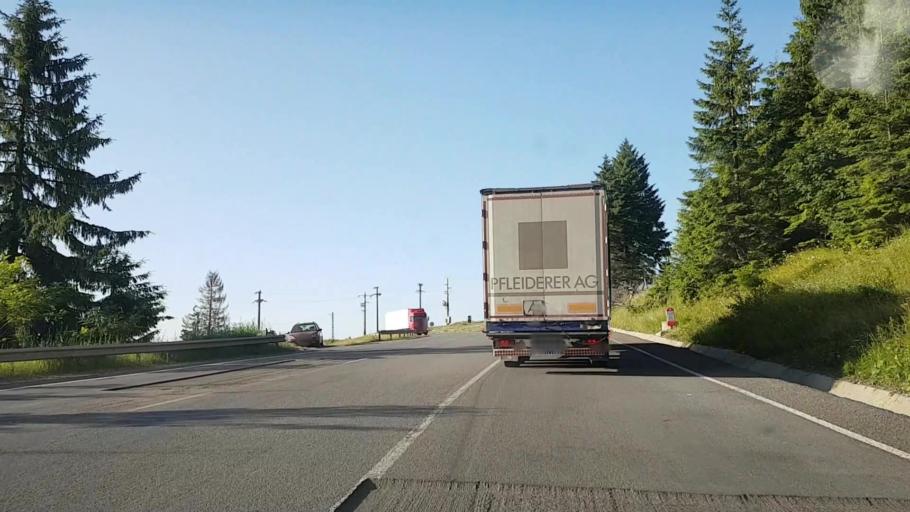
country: RO
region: Bistrita-Nasaud
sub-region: Comuna Lunca Ilvei
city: Lunca Ilvei
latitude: 47.2649
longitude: 25.0199
